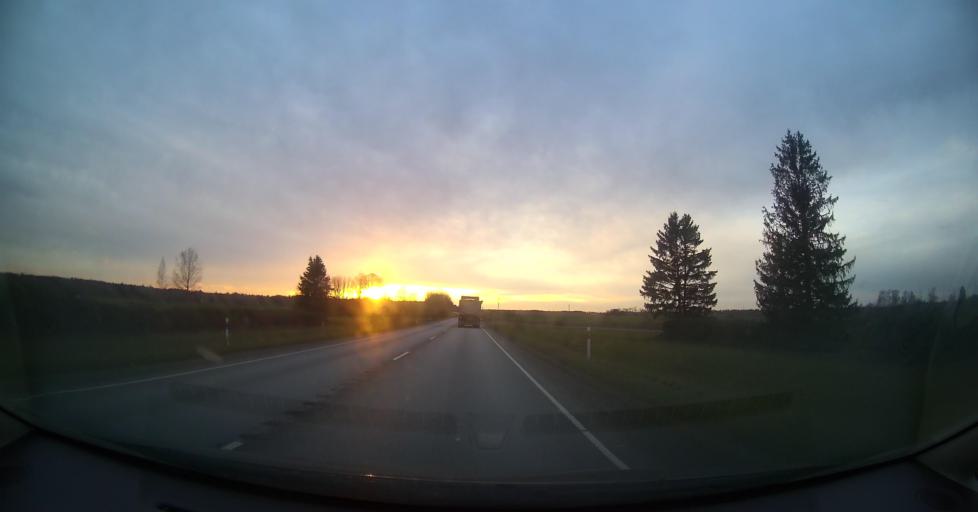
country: EE
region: Laeaene-Virumaa
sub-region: Viru-Nigula vald
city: Kunda
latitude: 59.4241
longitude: 26.6684
